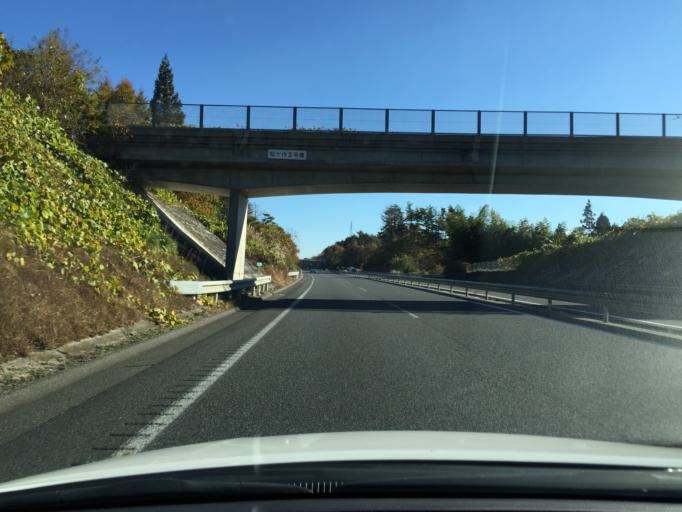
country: JP
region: Fukushima
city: Funehikimachi-funehiki
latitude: 37.4148
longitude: 140.5622
